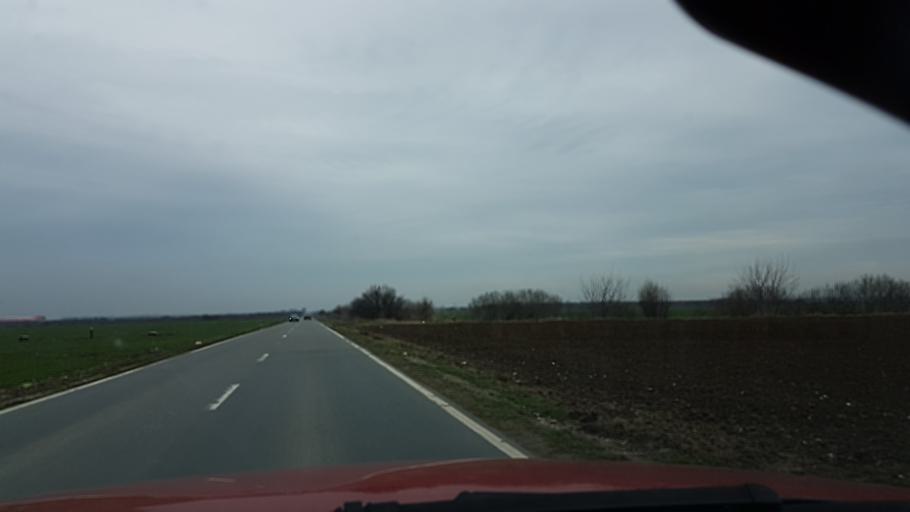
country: RO
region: Ilfov
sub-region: Comuna Tunari
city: Tunari
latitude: 44.5773
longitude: 26.1394
